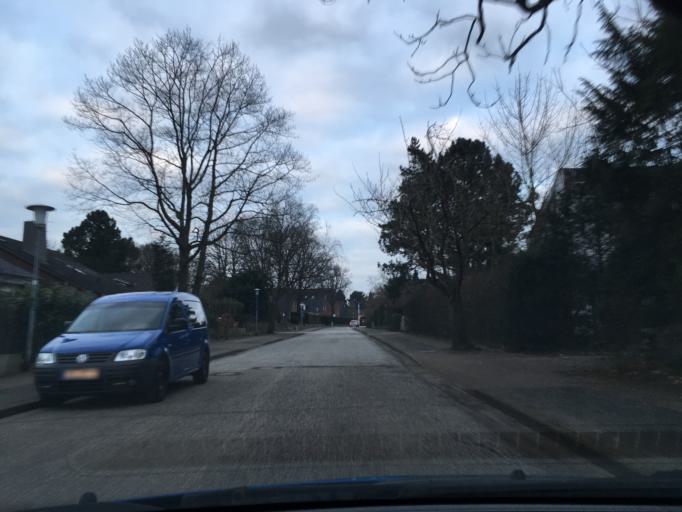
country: DE
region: Schleswig-Holstein
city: Wedel
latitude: 53.5898
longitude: 9.6996
